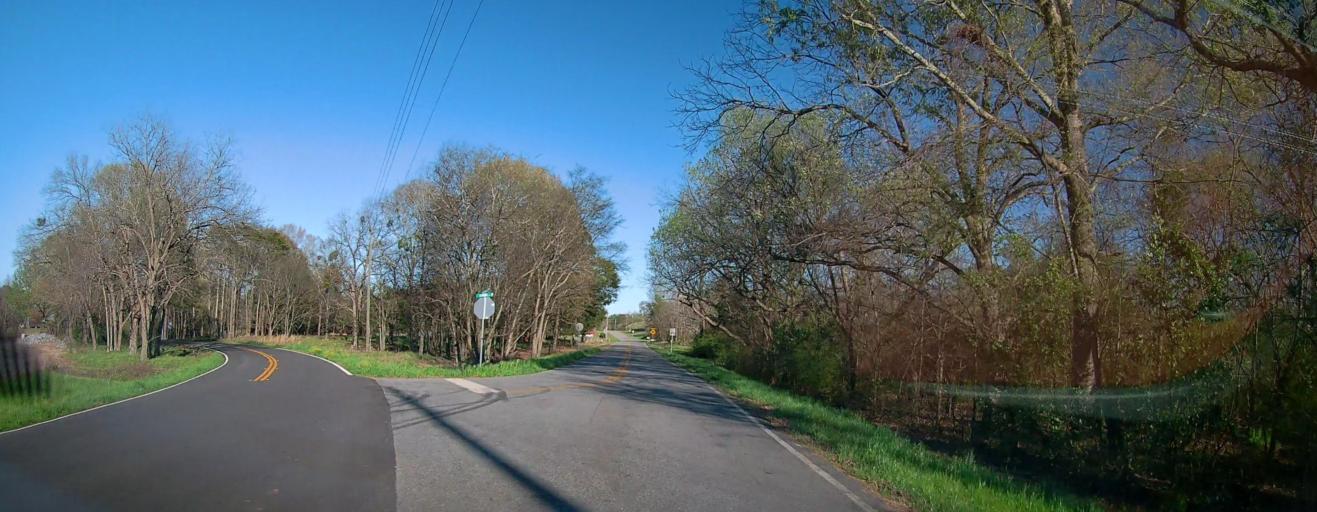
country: US
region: Georgia
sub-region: Houston County
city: Perry
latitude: 32.3641
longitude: -83.6658
